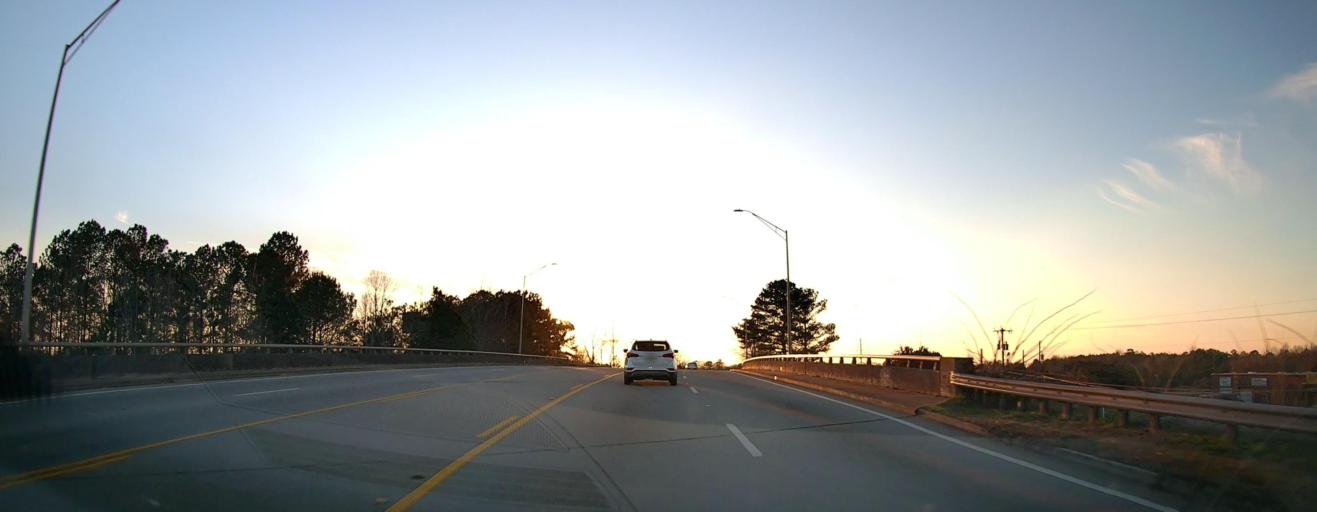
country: US
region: Georgia
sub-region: Troup County
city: La Grange
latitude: 33.0411
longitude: -84.9897
